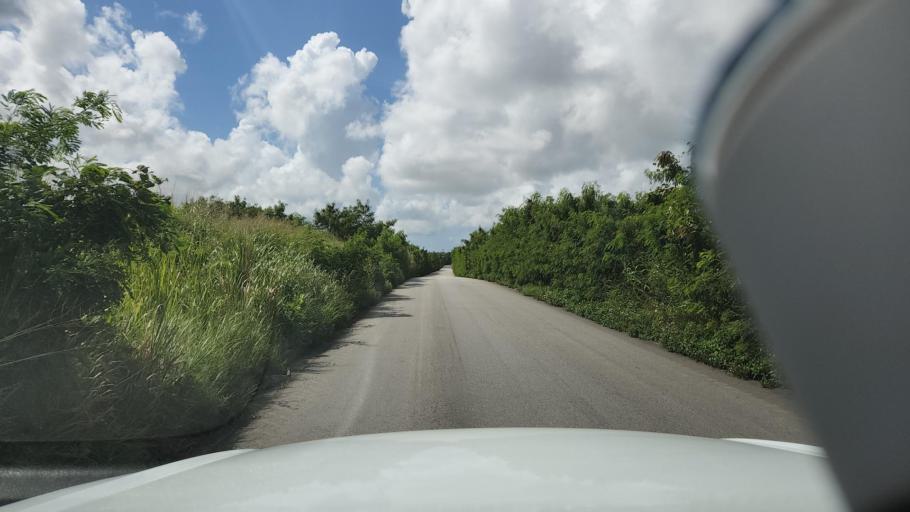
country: BB
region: Saint John
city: Four Cross Roads
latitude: 13.1669
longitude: -59.5085
